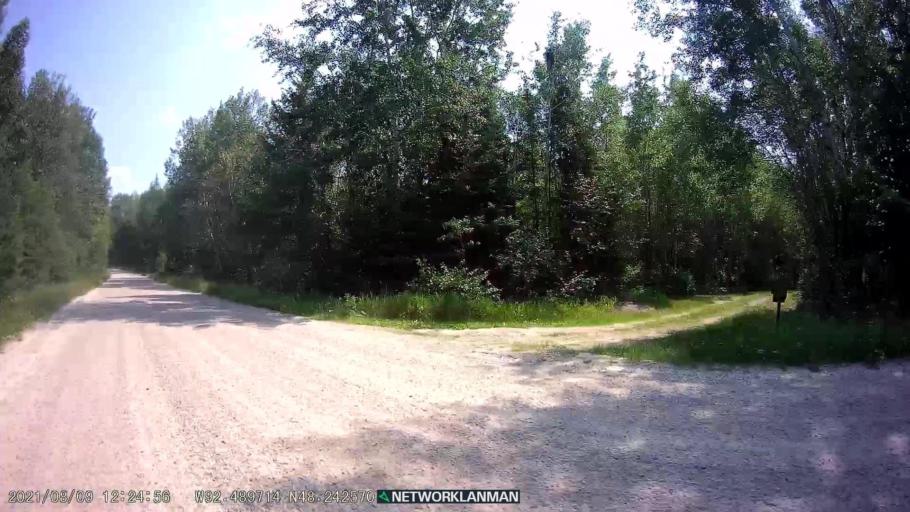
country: US
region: Minnesota
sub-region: Saint Louis County
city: Ely
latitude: 48.2425
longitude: -92.4895
